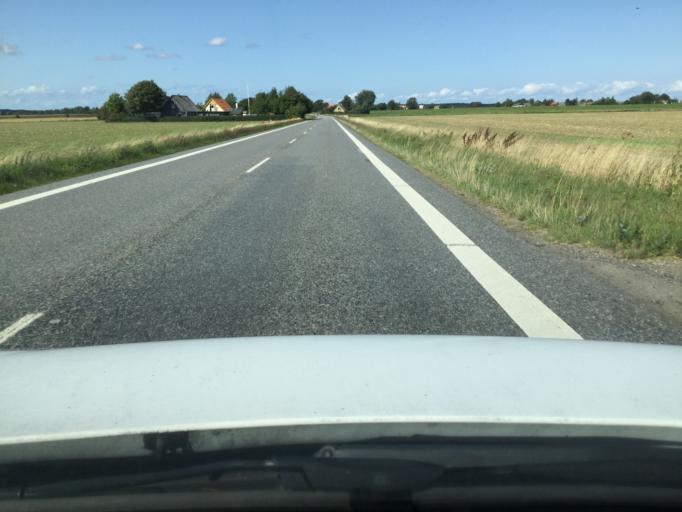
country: DK
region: Zealand
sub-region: Lolland Kommune
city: Rodby
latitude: 54.7392
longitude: 11.3893
